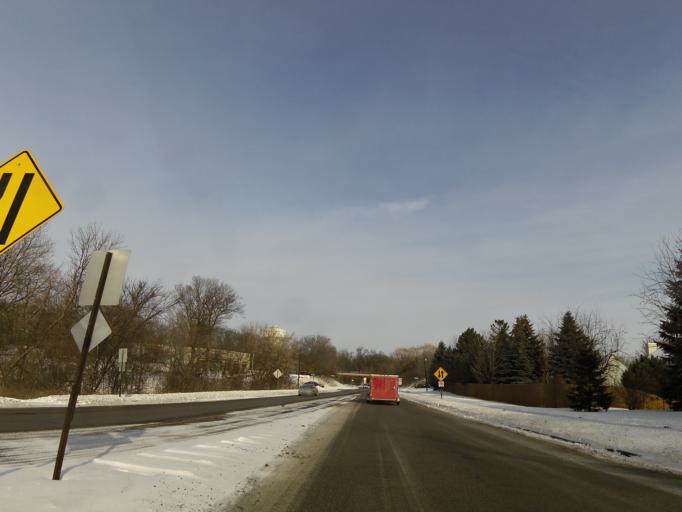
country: US
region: Minnesota
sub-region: Carver County
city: Chanhassen
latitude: 44.8652
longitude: -93.5113
